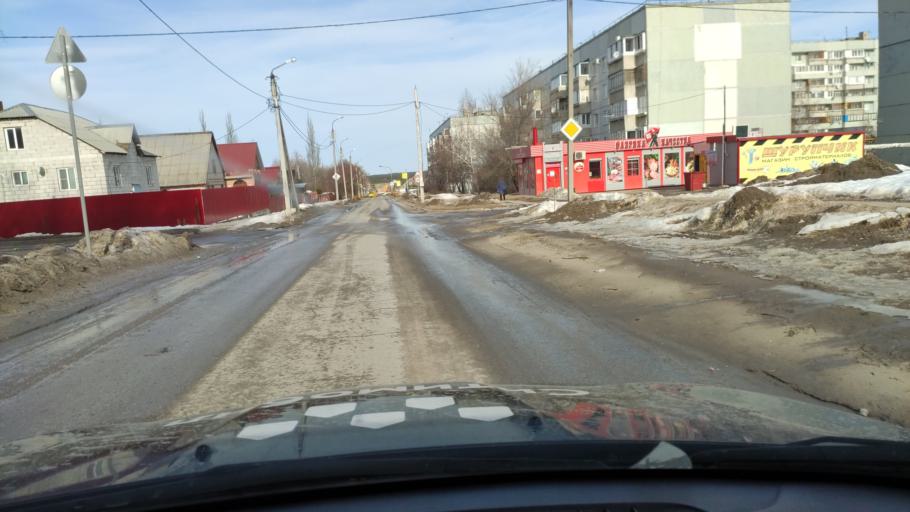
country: RU
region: Samara
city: Povolzhskiy
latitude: 53.5890
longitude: 49.7626
